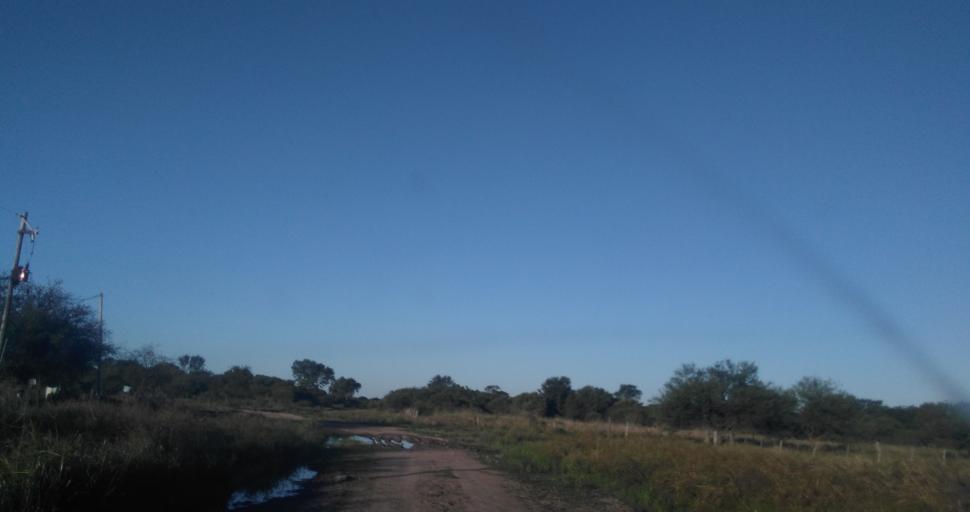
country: AR
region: Chaco
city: Fontana
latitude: -27.3867
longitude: -58.9738
